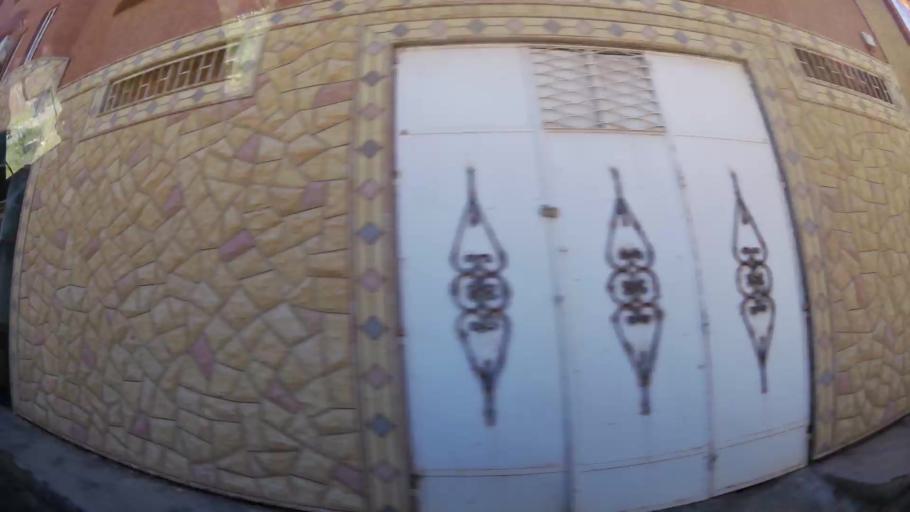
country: MA
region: Oriental
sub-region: Oujda-Angad
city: Oujda
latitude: 34.6770
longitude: -1.8630
